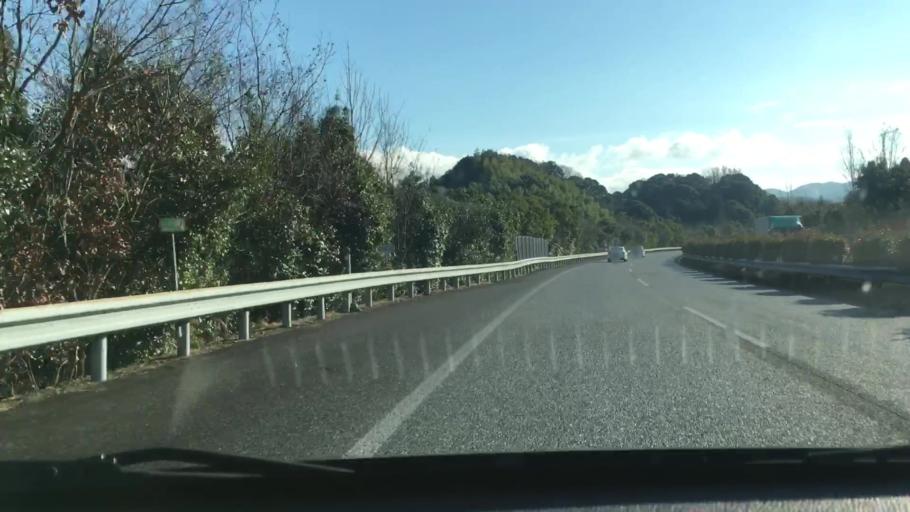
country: JP
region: Kumamoto
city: Hitoyoshi
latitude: 32.1957
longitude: 130.7779
